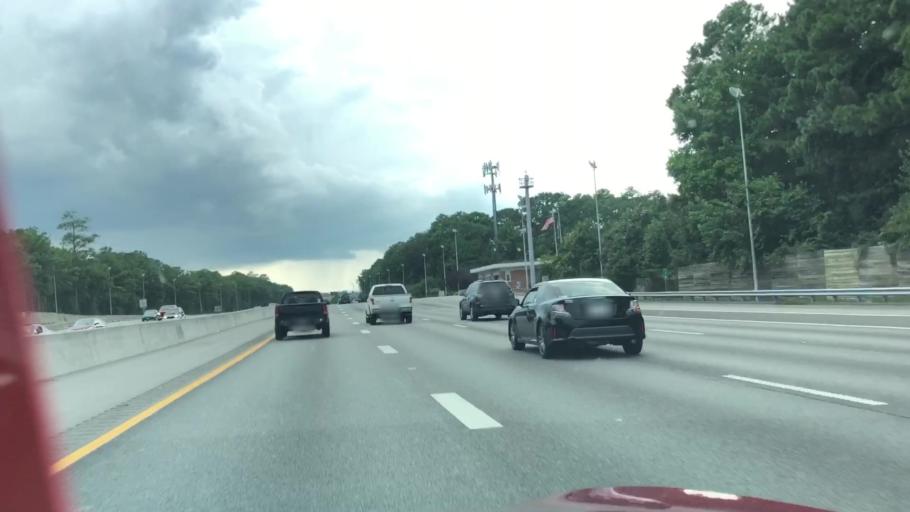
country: US
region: Virginia
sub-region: City of Virginia Beach
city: Virginia Beach
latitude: 36.8337
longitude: -76.1088
